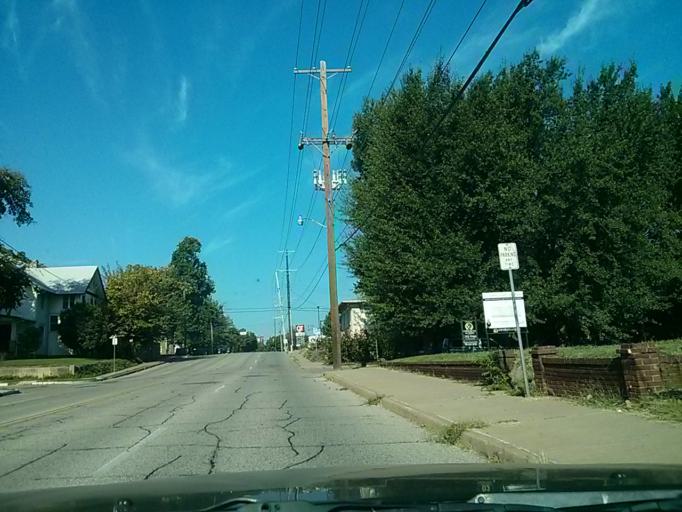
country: US
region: Oklahoma
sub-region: Tulsa County
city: Tulsa
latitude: 36.1406
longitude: -95.9902
